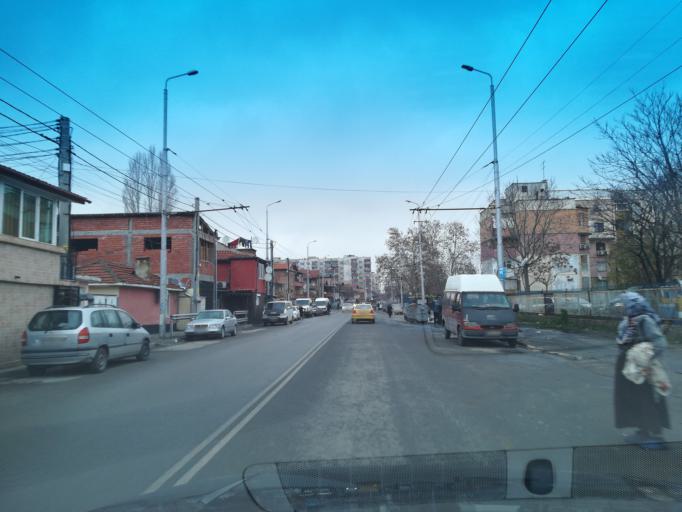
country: BG
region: Plovdiv
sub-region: Obshtina Plovdiv
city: Plovdiv
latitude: 42.1533
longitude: 24.7871
